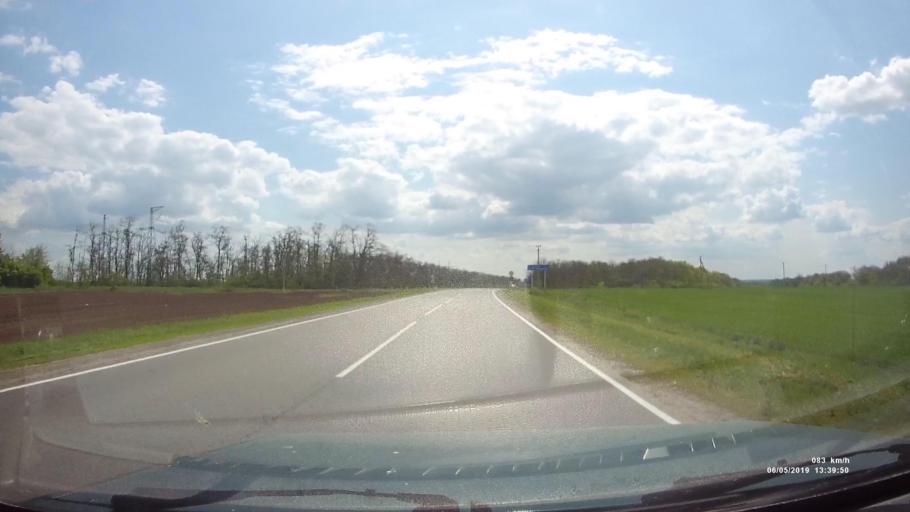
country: RU
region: Rostov
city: Ust'-Donetskiy
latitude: 47.6710
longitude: 40.7014
